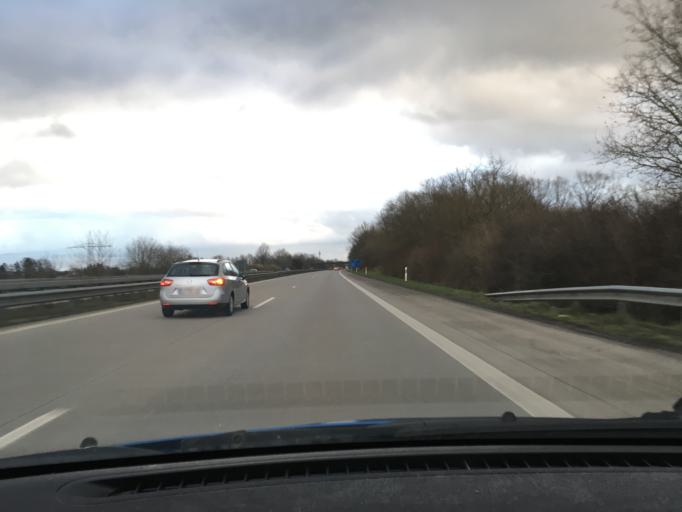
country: DE
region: Schleswig-Holstein
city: Klein Offenseth-Sparrieshoop
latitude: 53.8048
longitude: 9.6795
